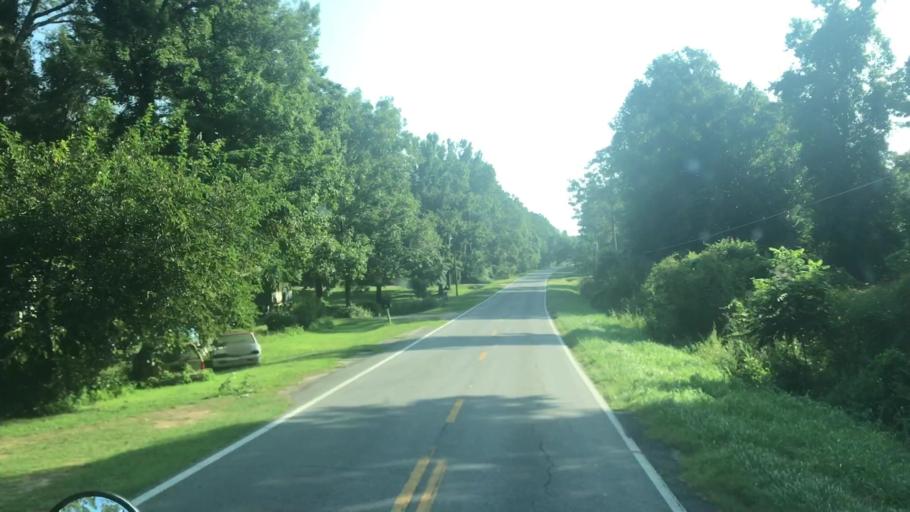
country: US
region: Florida
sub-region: Gadsden County
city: Quincy
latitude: 30.6535
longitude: -84.5679
